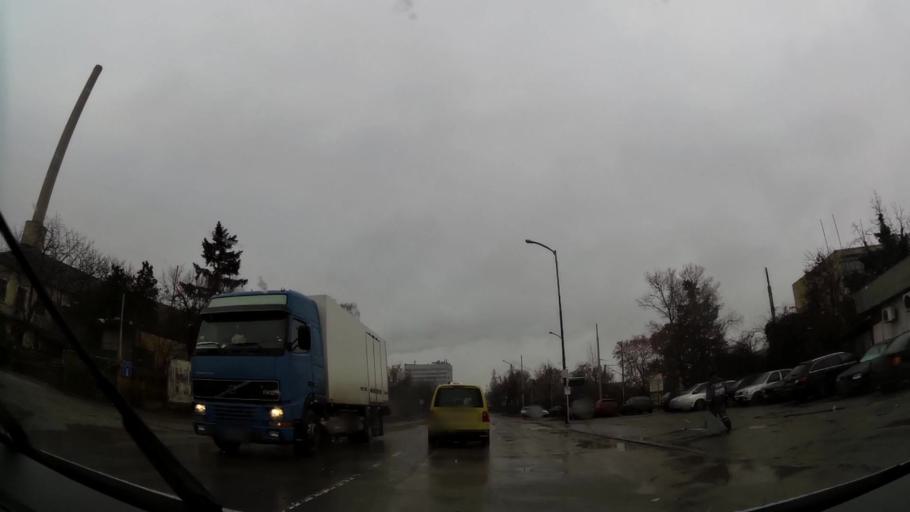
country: BG
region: Sofia-Capital
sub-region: Stolichna Obshtina
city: Sofia
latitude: 42.6622
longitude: 23.4156
